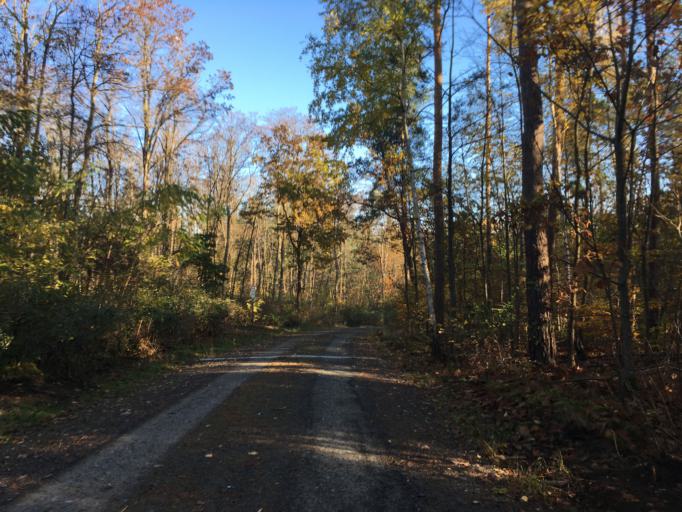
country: DE
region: Brandenburg
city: Wendisch Rietz
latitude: 52.1612
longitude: 13.9831
